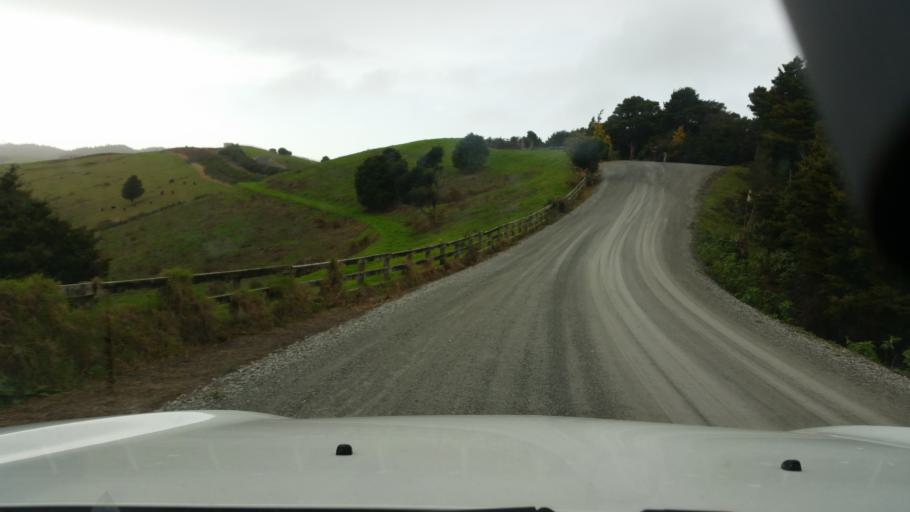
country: NZ
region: Northland
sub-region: Whangarei
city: Ngunguru
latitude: -35.7368
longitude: 174.4948
